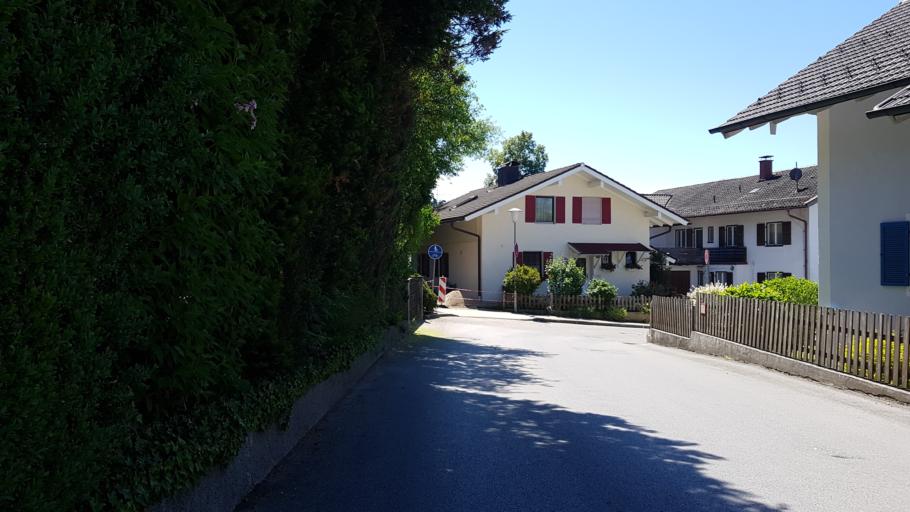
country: DE
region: Bavaria
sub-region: Upper Bavaria
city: Bad Endorf
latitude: 47.9056
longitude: 12.3050
